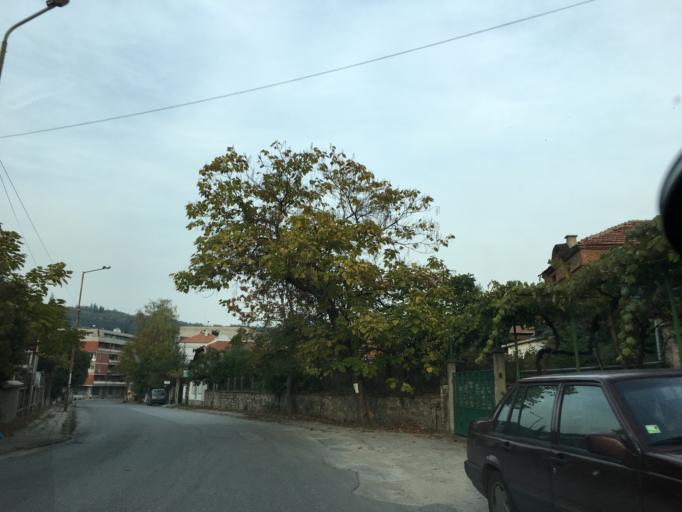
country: BG
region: Pazardzhik
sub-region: Obshtina Belovo
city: Belovo
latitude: 42.2122
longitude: 24.0148
